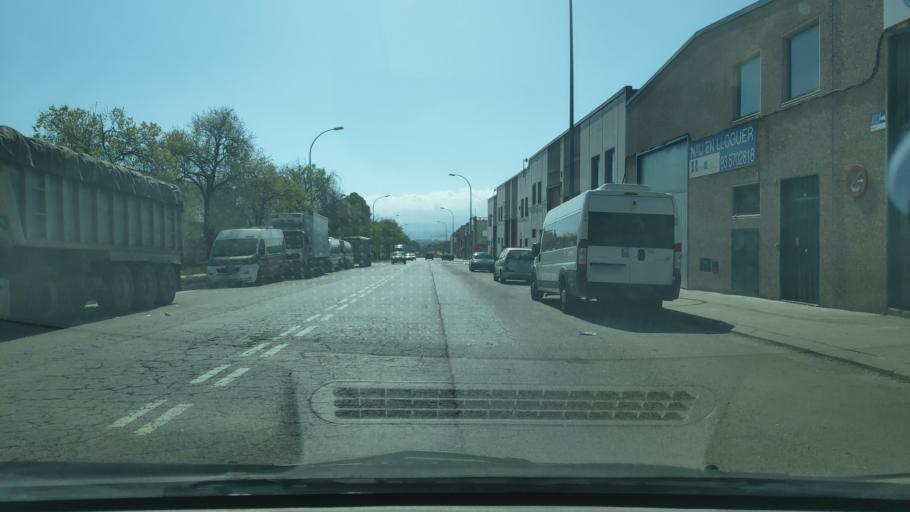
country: ES
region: Catalonia
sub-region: Provincia de Barcelona
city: Polinya
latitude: 41.5369
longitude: 2.1329
